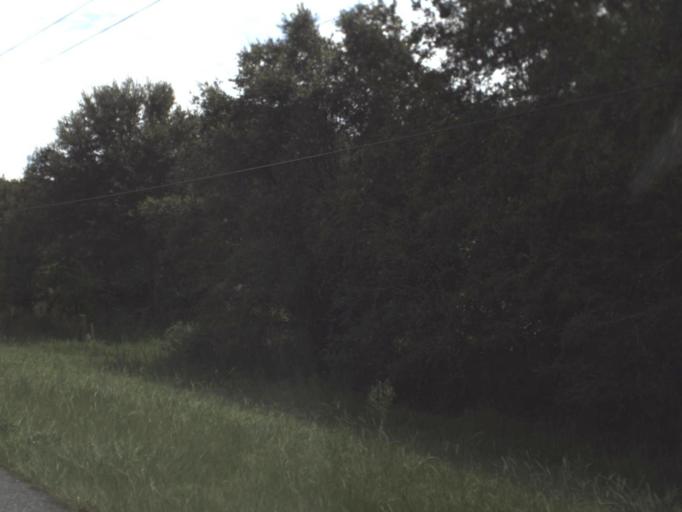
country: US
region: Florida
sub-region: Citrus County
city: Hernando
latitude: 28.9574
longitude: -82.3776
